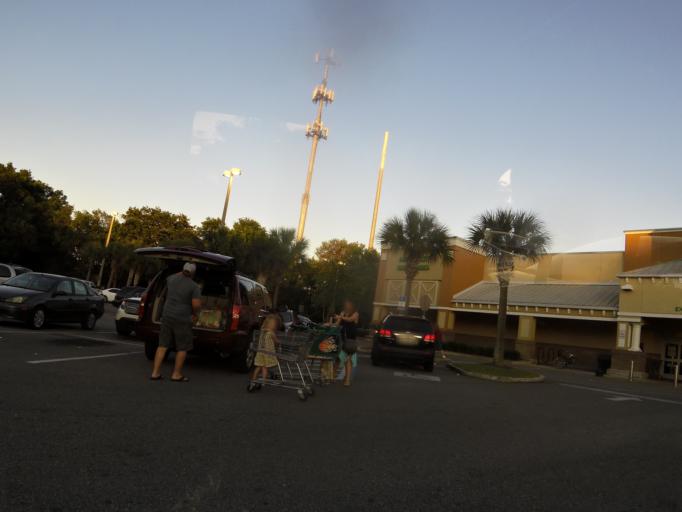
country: US
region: Florida
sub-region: Duval County
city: Jacksonville
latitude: 30.3129
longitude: -81.6018
